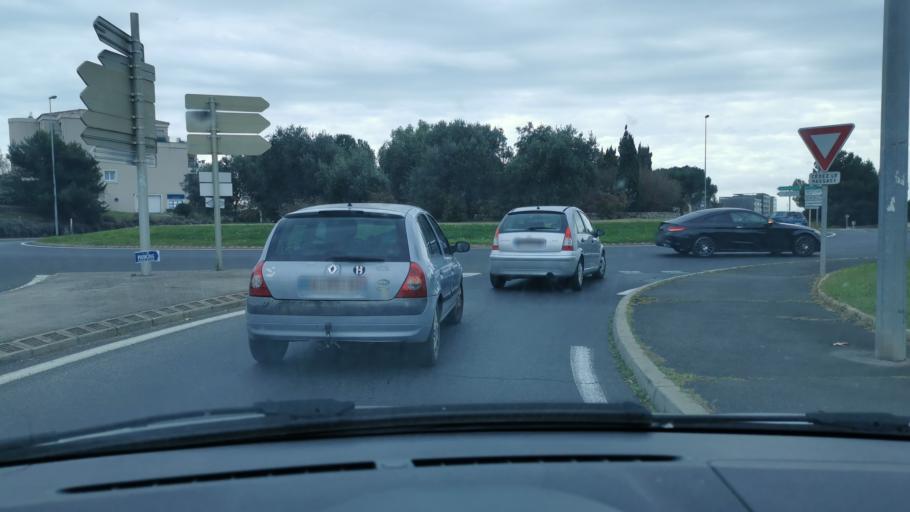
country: FR
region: Languedoc-Roussillon
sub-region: Departement de l'Herault
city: Sete
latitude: 43.4019
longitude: 3.6620
